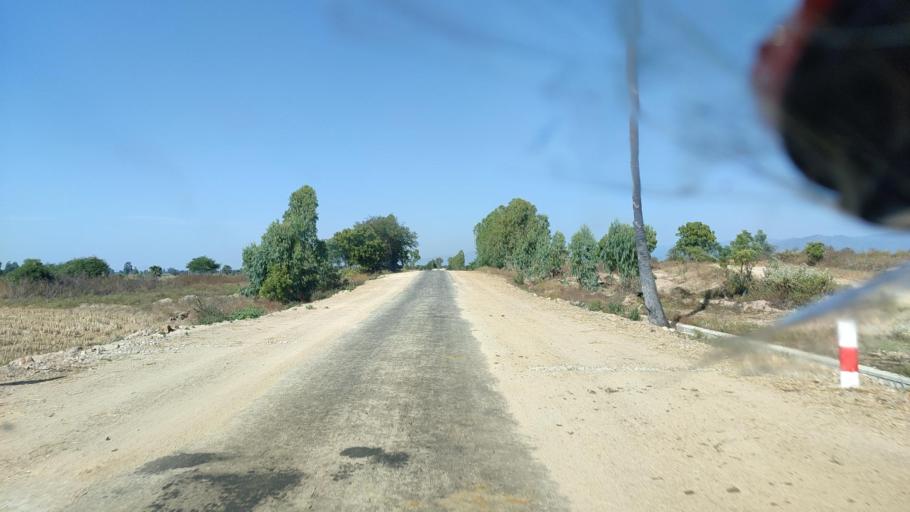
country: MM
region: Mandalay
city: Pyinmana
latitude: 20.0900
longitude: 96.2644
